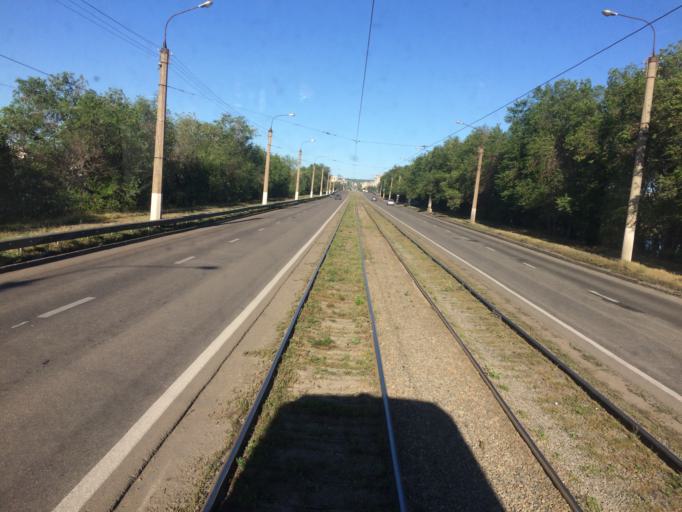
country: RU
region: Chelyabinsk
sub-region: Gorod Magnitogorsk
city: Magnitogorsk
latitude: 53.3981
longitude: 59.0071
